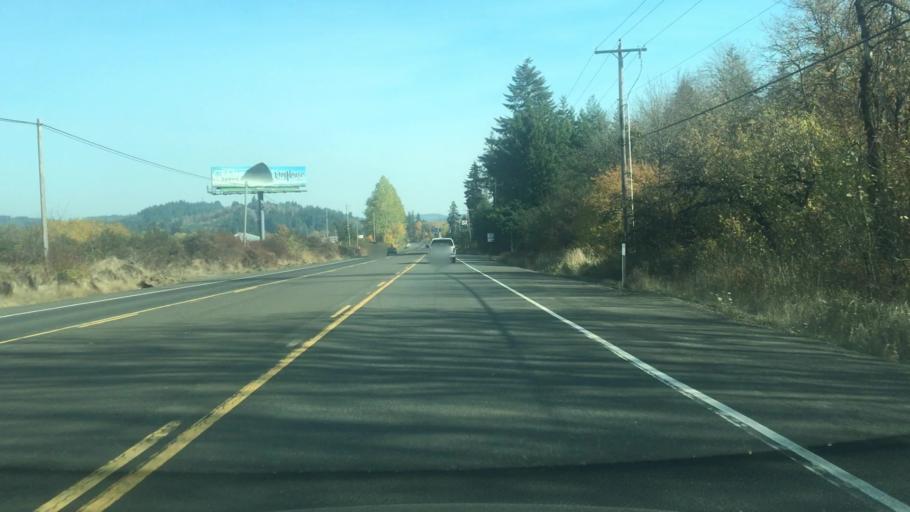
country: US
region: Oregon
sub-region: Polk County
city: Grand Ronde
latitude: 45.0583
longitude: -123.6246
